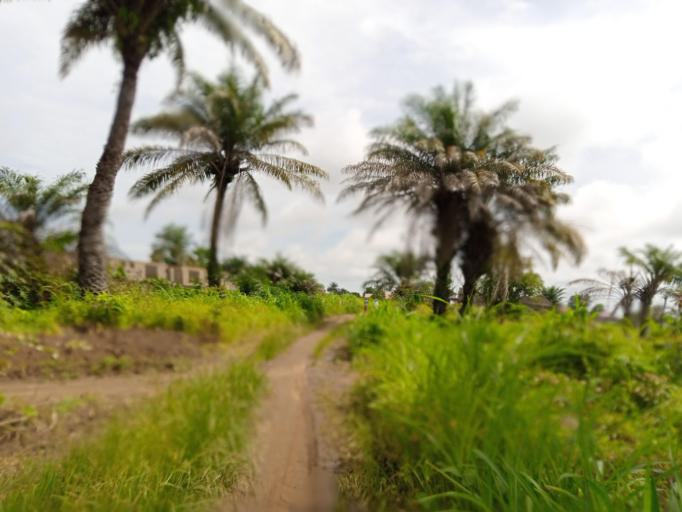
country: SL
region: Northern Province
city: Masoyila
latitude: 8.5897
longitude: -13.1946
